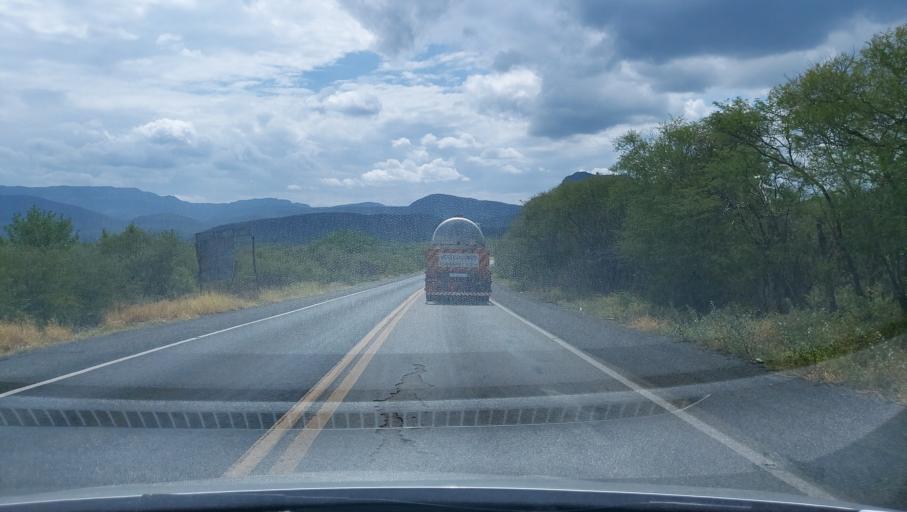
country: BR
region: Bahia
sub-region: Oliveira Dos Brejinhos
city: Beira Rio
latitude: -12.3815
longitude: -42.4140
